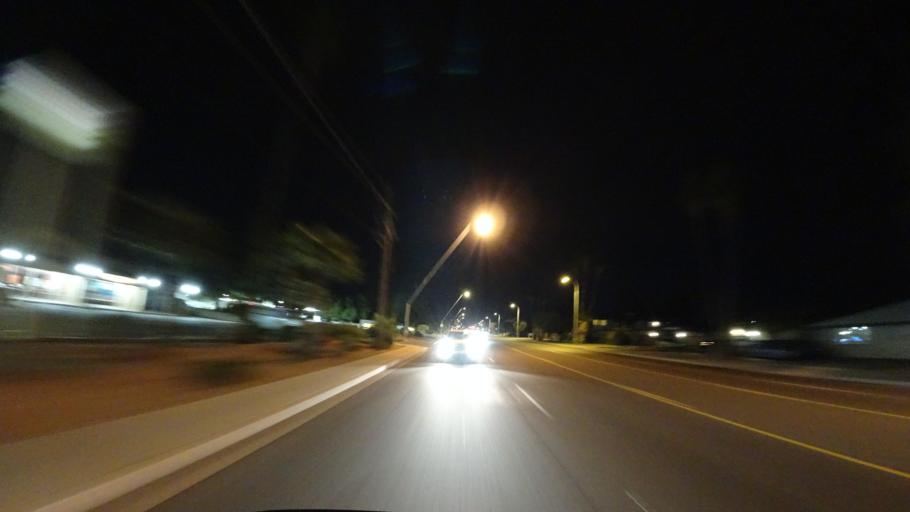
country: US
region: Arizona
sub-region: Maricopa County
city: Chandler
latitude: 33.3207
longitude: -111.8477
